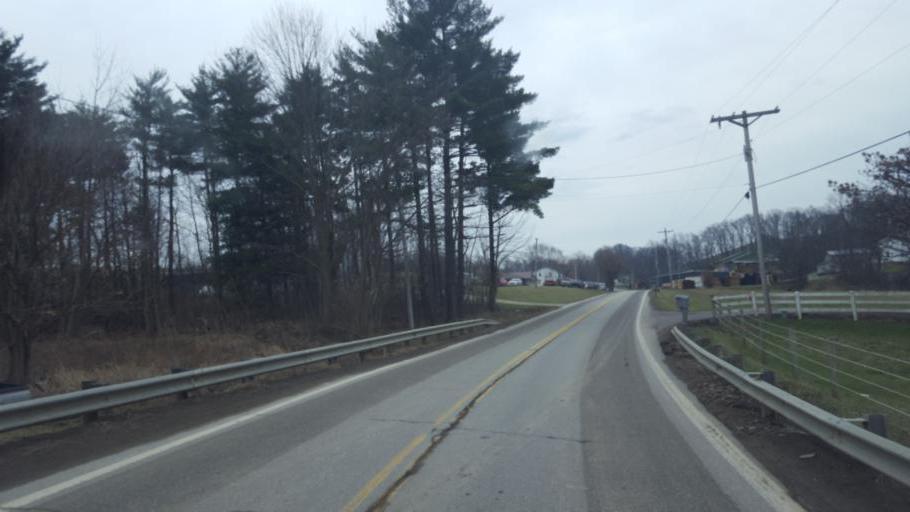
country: US
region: Ohio
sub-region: Tuscarawas County
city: Sugarcreek
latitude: 40.5022
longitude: -81.7774
